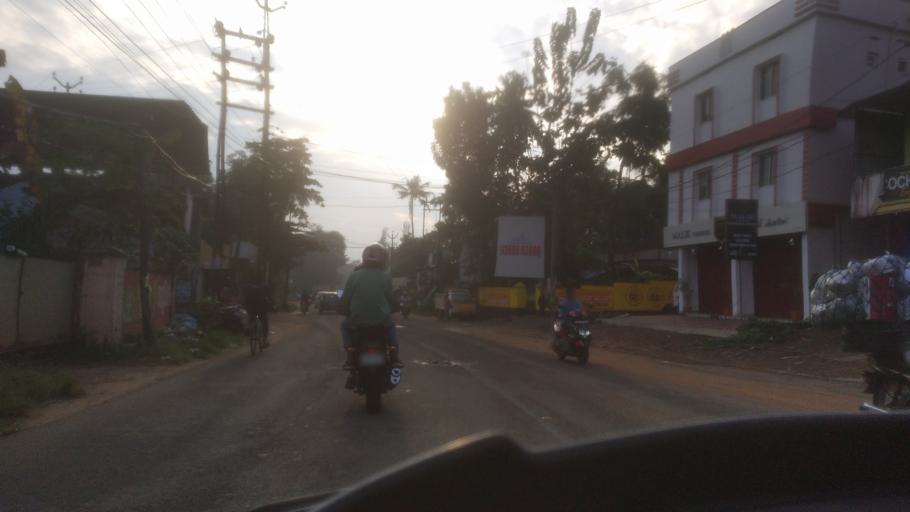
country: IN
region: Kerala
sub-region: Ernakulam
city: Perumpavur
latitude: 10.1164
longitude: 76.4602
